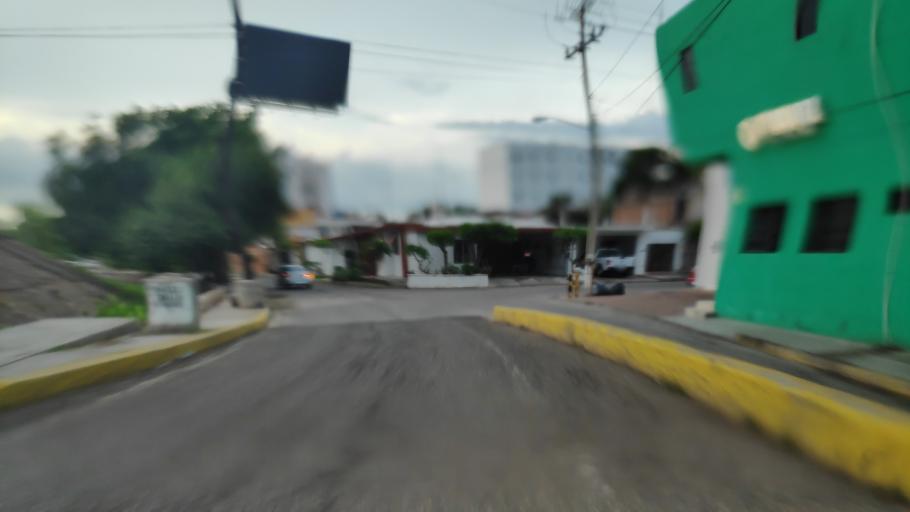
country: MX
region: Sinaloa
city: Culiacan
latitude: 24.8075
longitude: -107.4060
